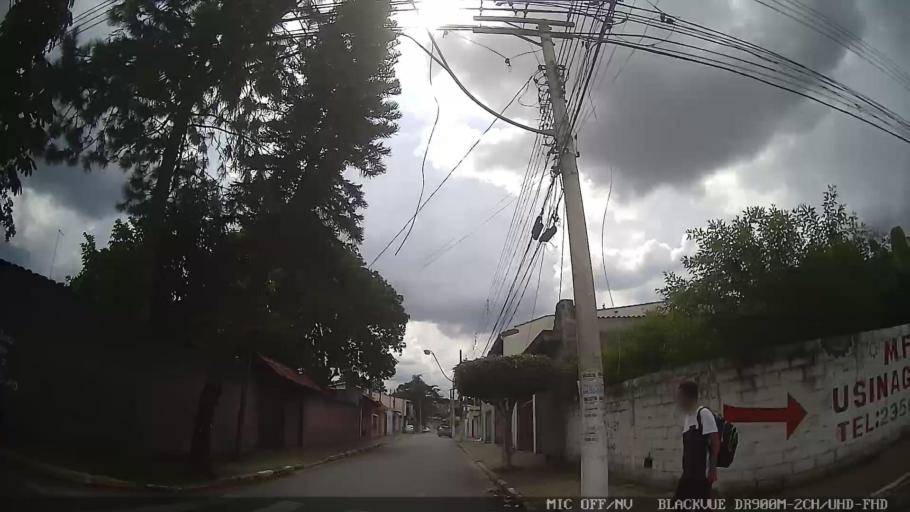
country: BR
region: Sao Paulo
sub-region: Poa
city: Poa
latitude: -23.5356
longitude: -46.3392
